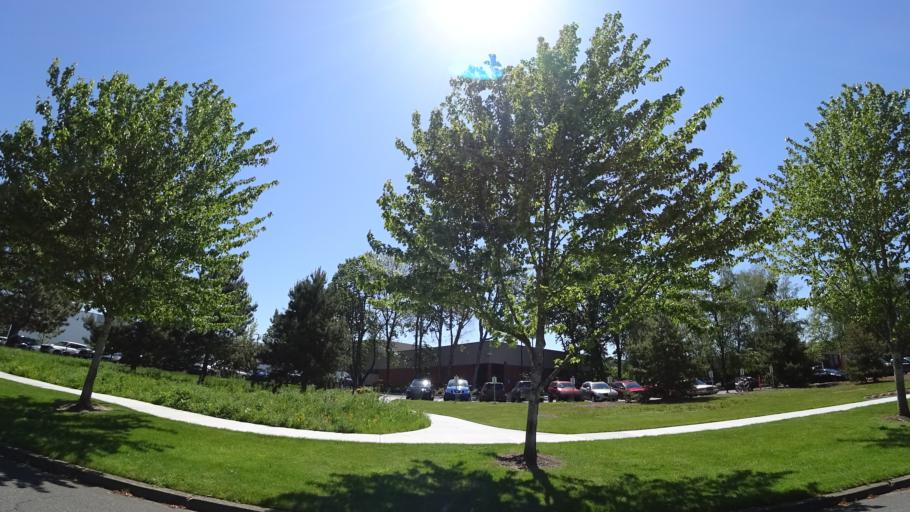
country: US
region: Oregon
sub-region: Washington County
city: Beaverton
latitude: 45.4973
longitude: -122.8168
